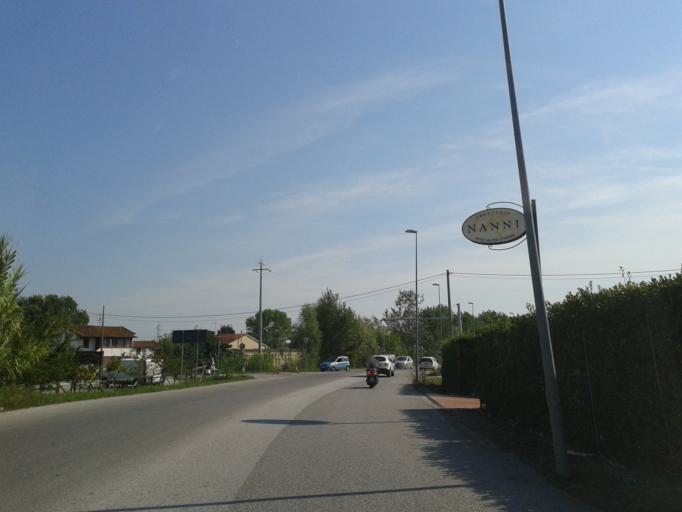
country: IT
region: Tuscany
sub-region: Provincia di Lucca
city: Camaiore
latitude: 43.8959
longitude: 10.2526
